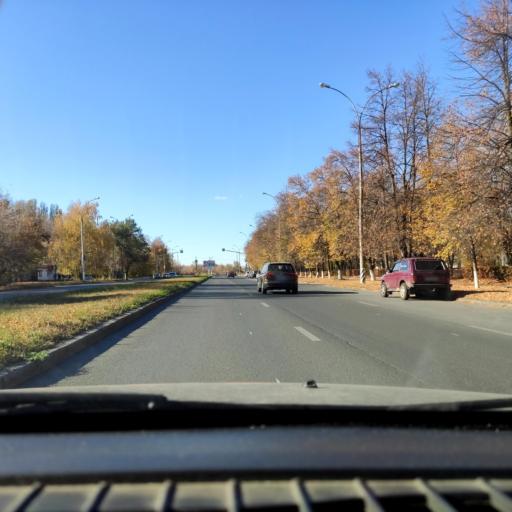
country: RU
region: Samara
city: Tol'yatti
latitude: 53.5163
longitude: 49.2640
